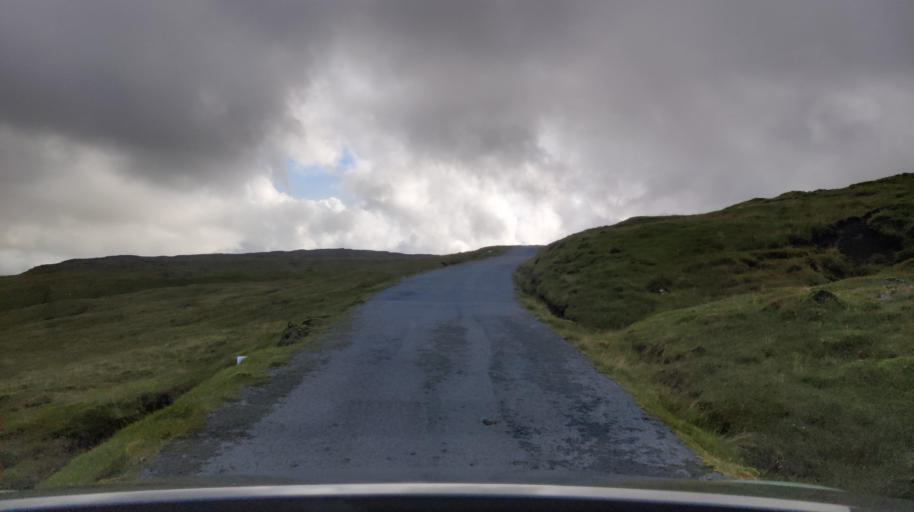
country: FO
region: Streymoy
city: Vestmanna
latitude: 62.1736
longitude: -7.1559
